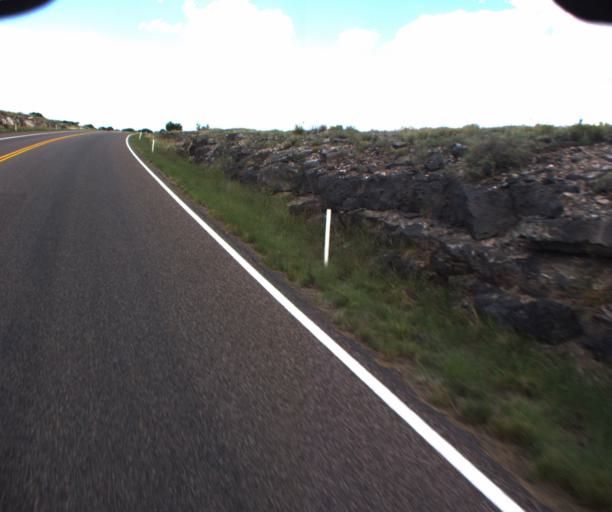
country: US
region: Arizona
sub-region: Apache County
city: Springerville
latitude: 34.1437
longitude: -109.2241
